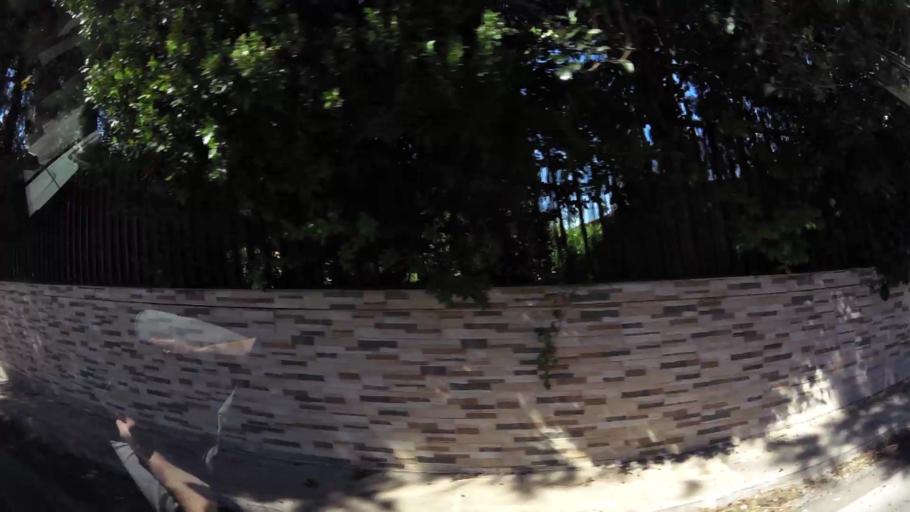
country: GR
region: Attica
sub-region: Nomarchia Athinas
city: Kifisia
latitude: 38.0826
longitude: 23.7969
